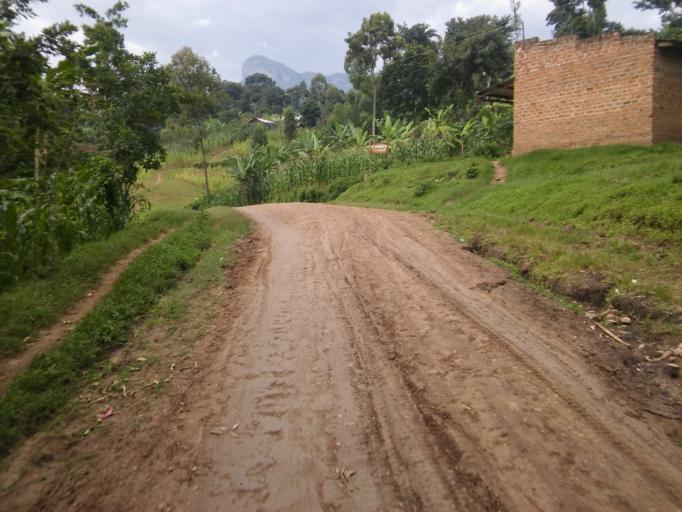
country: UG
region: Eastern Region
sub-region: Manafwa District
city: Manafwa
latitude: 0.8923
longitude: 34.3613
